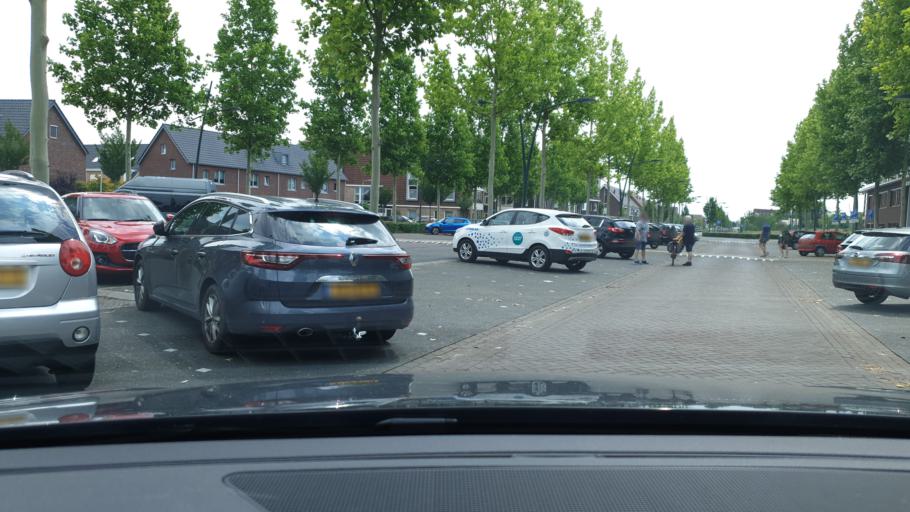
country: NL
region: Gelderland
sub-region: Gemeente Overbetuwe
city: Elst
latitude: 51.9223
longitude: 5.8617
